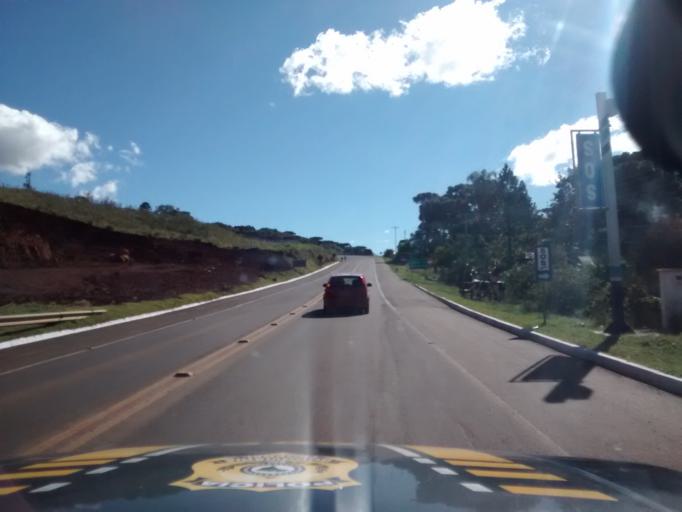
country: BR
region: Rio Grande do Sul
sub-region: Vacaria
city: Vacaria
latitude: -28.3245
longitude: -51.1904
